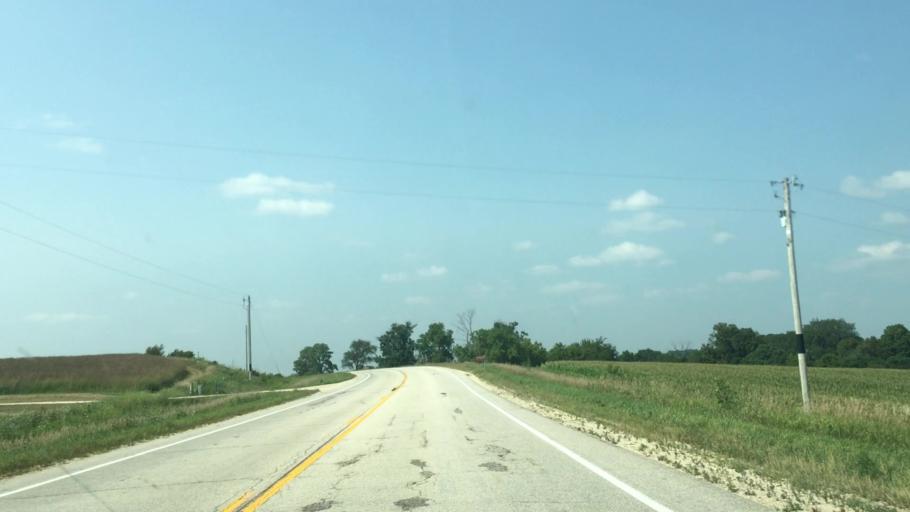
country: US
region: Minnesota
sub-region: Fillmore County
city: Harmony
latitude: 43.6768
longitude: -91.9396
